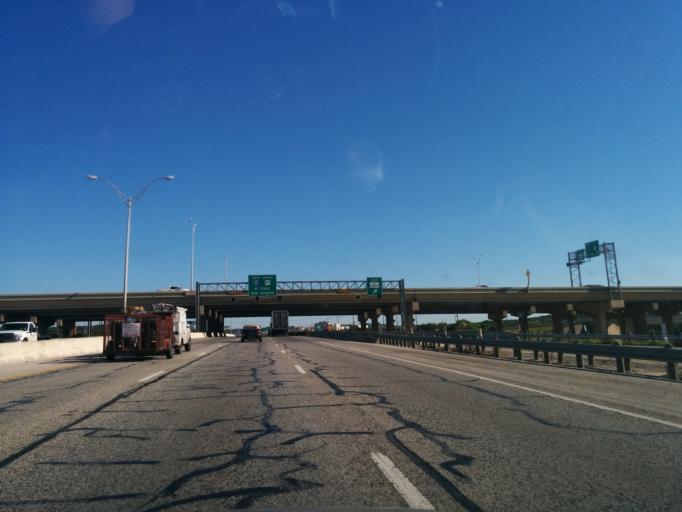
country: US
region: Texas
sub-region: Bexar County
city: Shavano Park
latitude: 29.5896
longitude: -98.5982
